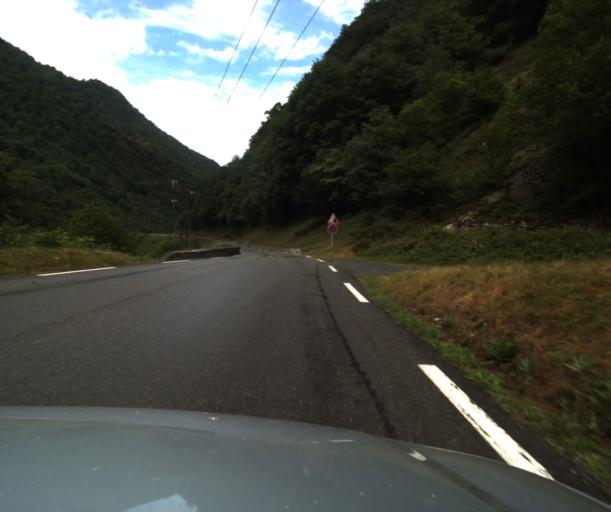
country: FR
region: Midi-Pyrenees
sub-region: Departement des Hautes-Pyrenees
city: Luz-Saint-Sauveur
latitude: 42.8416
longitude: -0.0059
